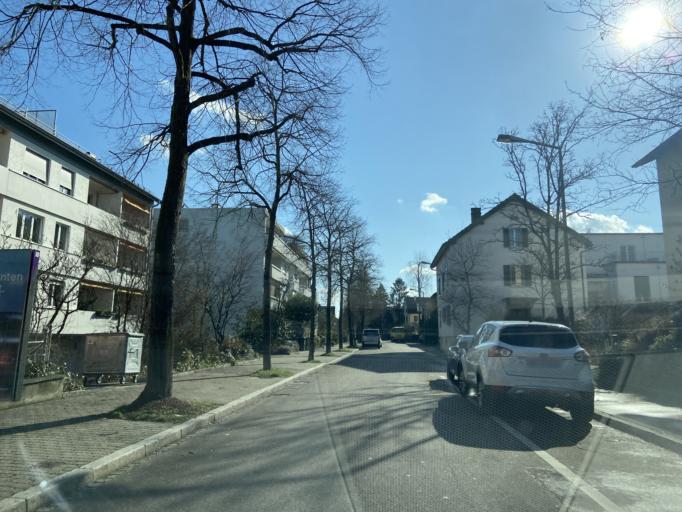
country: CH
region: Zurich
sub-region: Bezirk Winterthur
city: Wuelflingen (Kreis 6) / Lindenplatz
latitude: 47.5084
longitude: 8.6979
